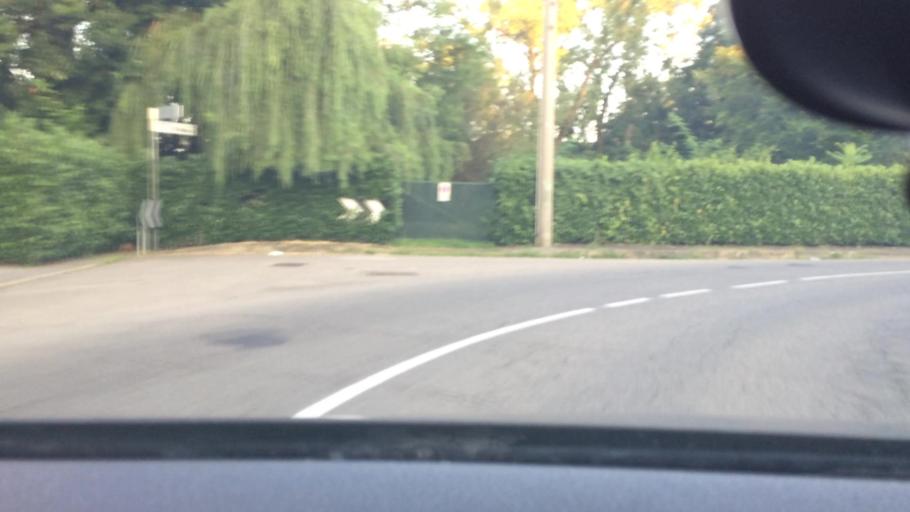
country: IT
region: Lombardy
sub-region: Provincia di Como
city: Rovello Porro
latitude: 45.6519
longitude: 9.0446
